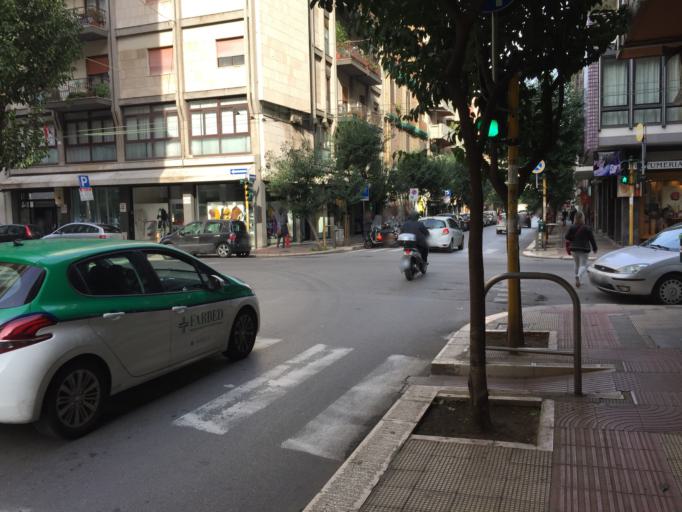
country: IT
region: Apulia
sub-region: Provincia di Bari
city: Bari
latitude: 41.1222
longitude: 16.8655
